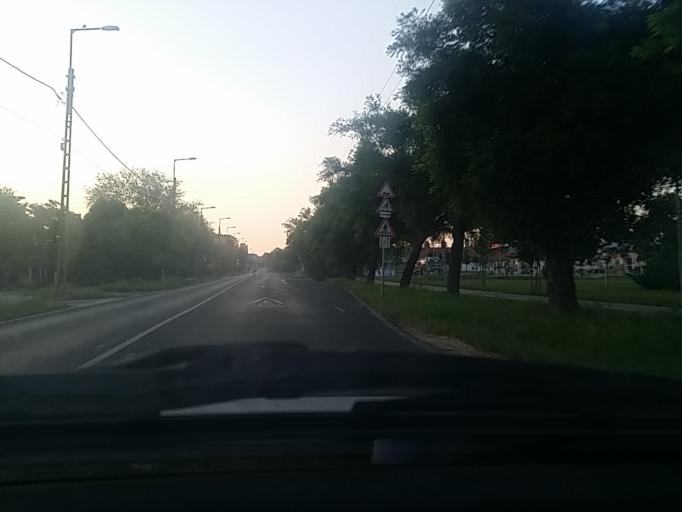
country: HU
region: Budapest
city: Budapest XVII. keruelet
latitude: 47.4740
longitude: 19.2723
